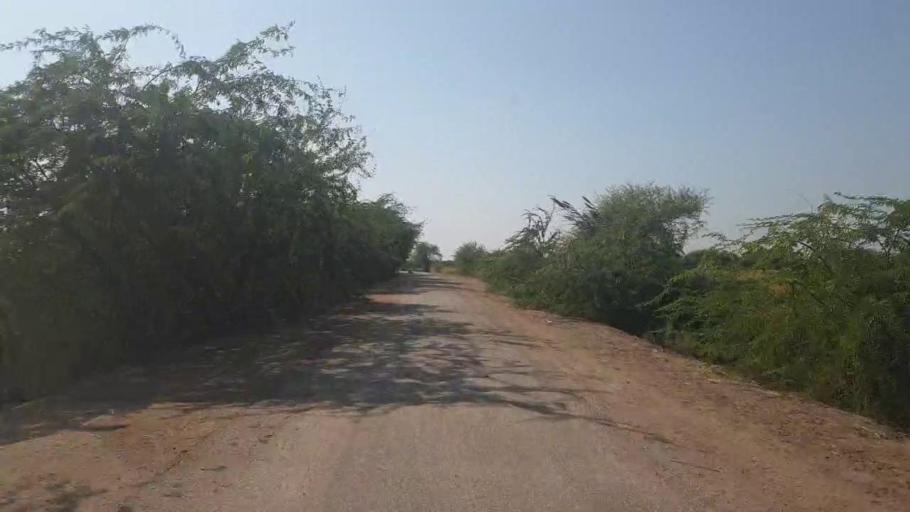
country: PK
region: Sindh
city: Badin
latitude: 24.5548
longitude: 68.8210
